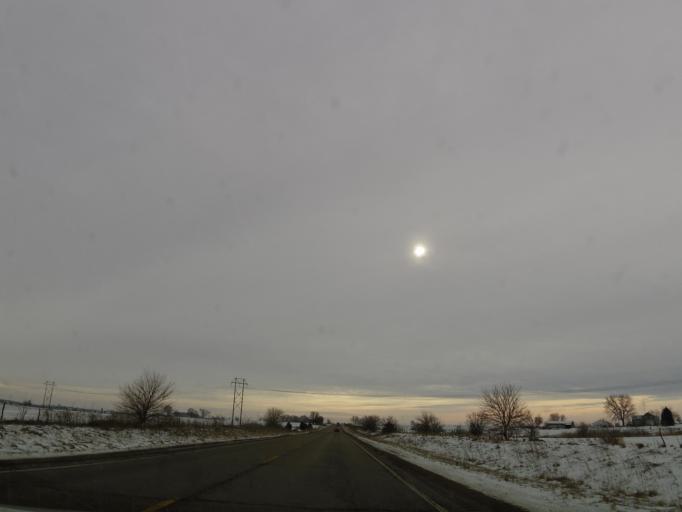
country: US
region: Illinois
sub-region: LaSalle County
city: Oglesby
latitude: 41.2911
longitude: -89.0970
